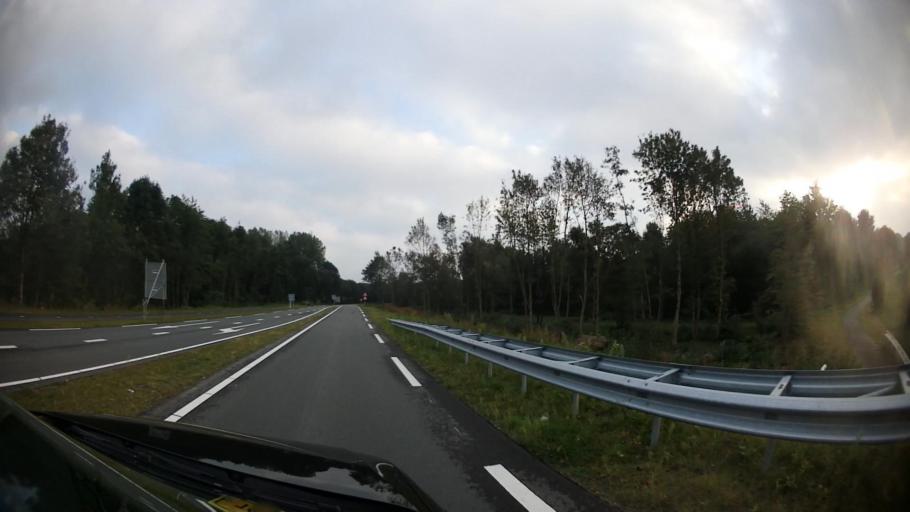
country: NL
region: Flevoland
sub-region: Gemeente Almere
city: Almere Stad
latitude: 52.3480
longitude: 5.1981
